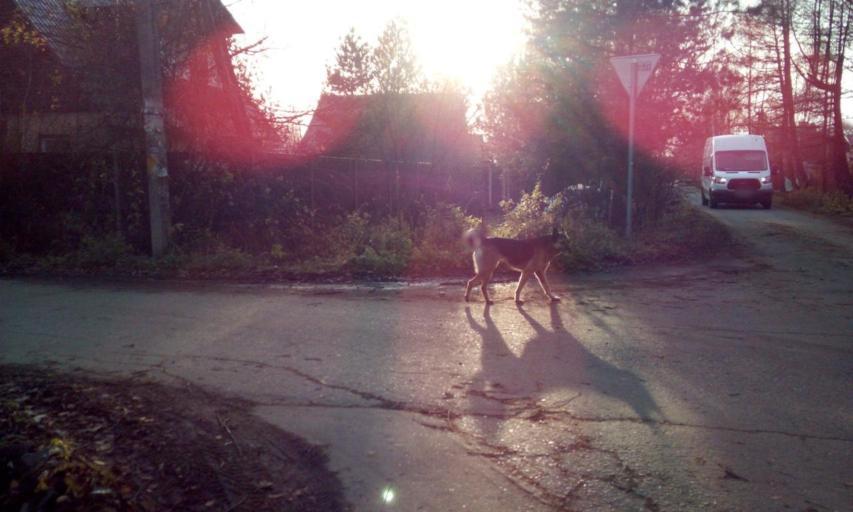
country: RU
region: Moskovskaya
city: Aprelevka
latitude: 55.5624
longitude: 37.0964
